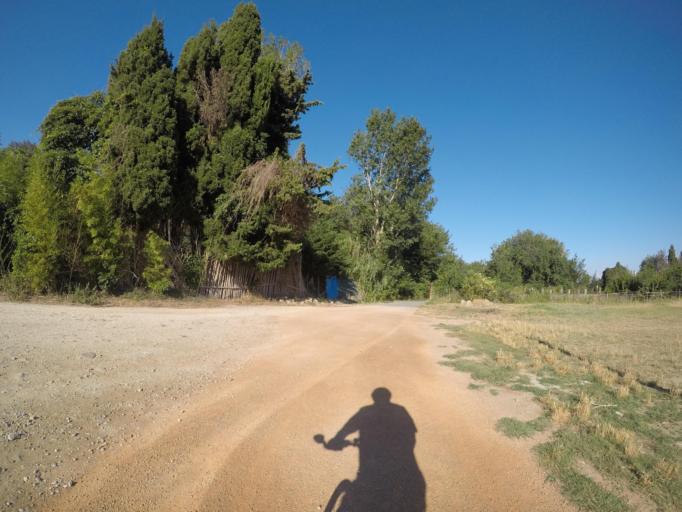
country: FR
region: Languedoc-Roussillon
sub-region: Departement des Pyrenees-Orientales
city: Pezilla-la-Riviere
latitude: 42.6807
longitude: 2.7544
